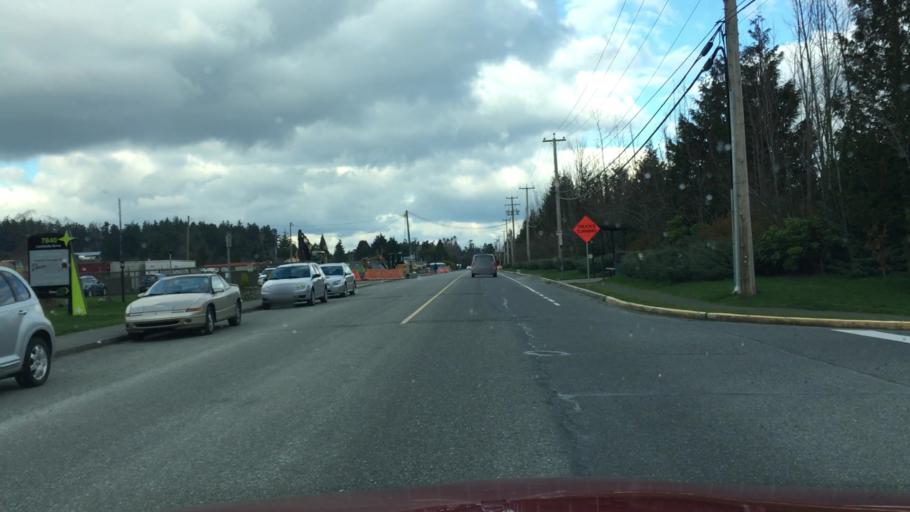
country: CA
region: British Columbia
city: North Saanich
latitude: 48.5952
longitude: -123.3946
